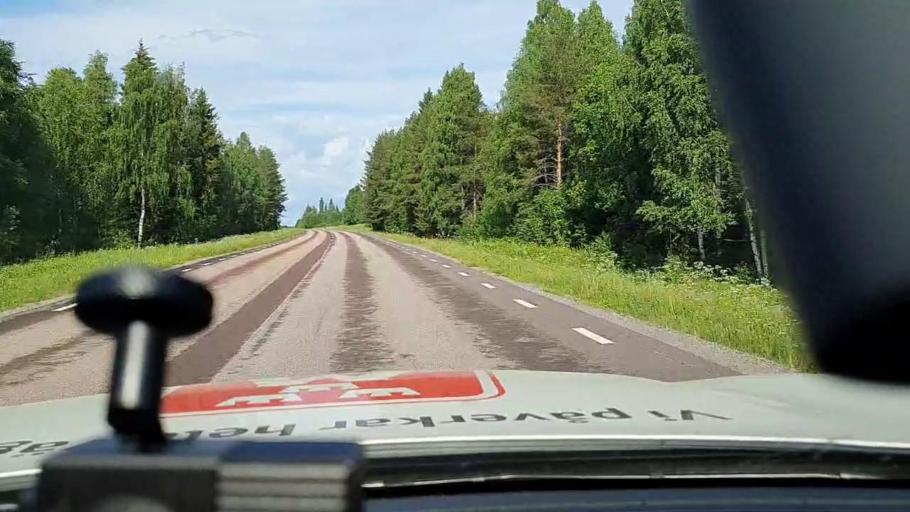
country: SE
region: Norrbotten
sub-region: Alvsbyns Kommun
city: AElvsbyn
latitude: 66.0219
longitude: 21.1311
